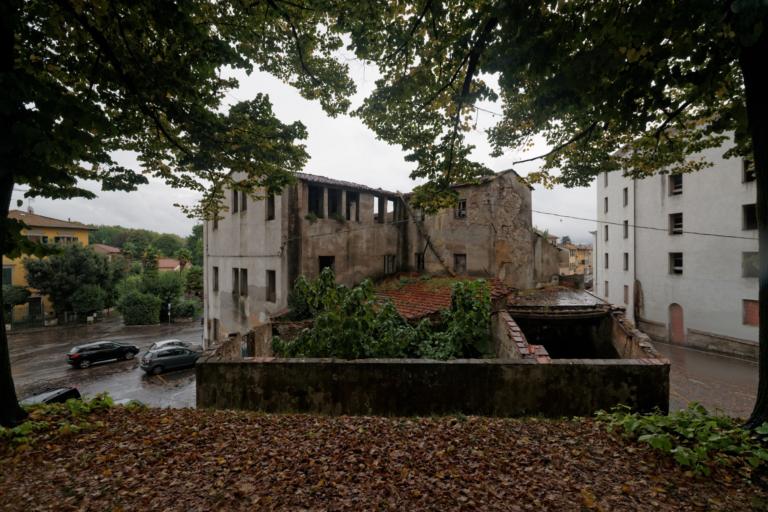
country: IT
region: Tuscany
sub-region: Provincia di Lucca
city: Lucca
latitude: 43.8485
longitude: 10.5122
